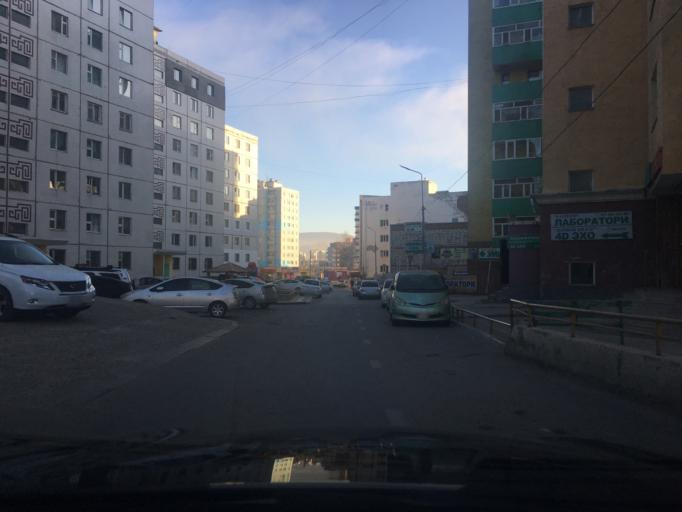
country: MN
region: Ulaanbaatar
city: Ulaanbaatar
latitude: 47.9198
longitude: 106.8852
